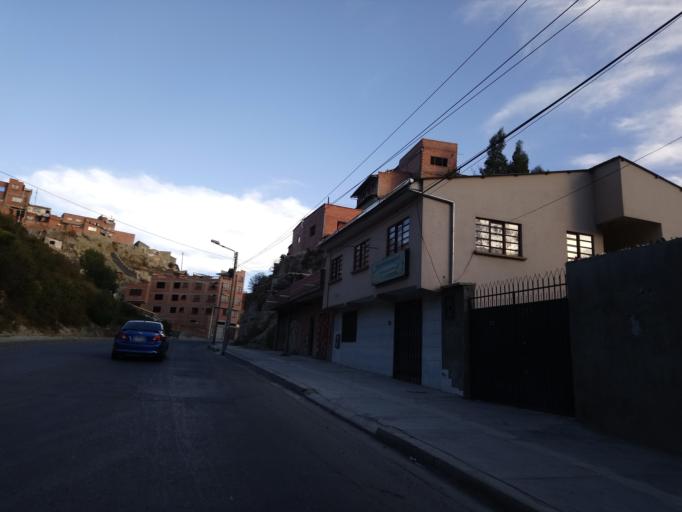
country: BO
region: La Paz
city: La Paz
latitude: -16.4843
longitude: -68.1379
